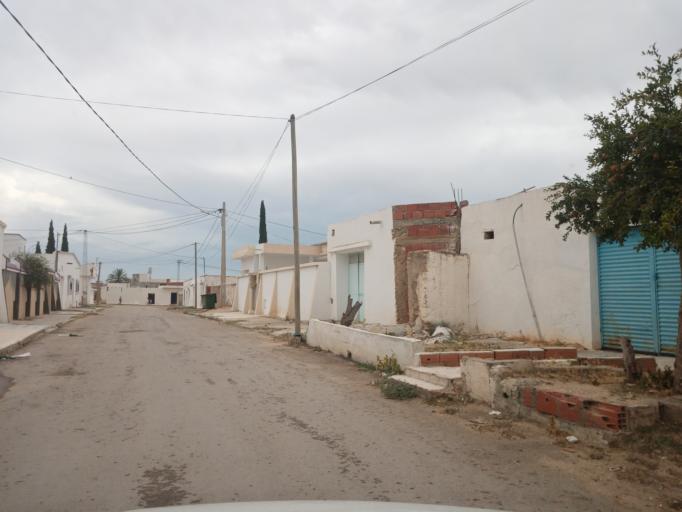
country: TN
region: Al Qayrawan
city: Sbikha
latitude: 36.1159
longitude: 10.0908
